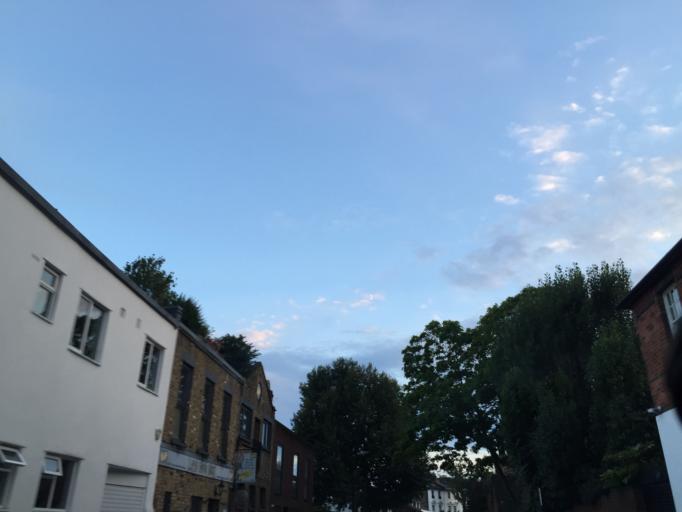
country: GB
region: England
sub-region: Greater London
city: Belsize Park
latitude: 51.5480
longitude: -0.1732
